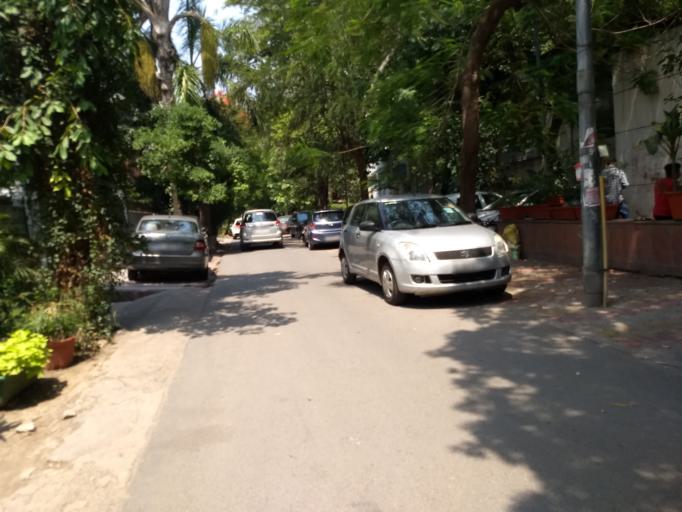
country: IN
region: NCT
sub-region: New Delhi
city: New Delhi
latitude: 28.5591
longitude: 77.2151
